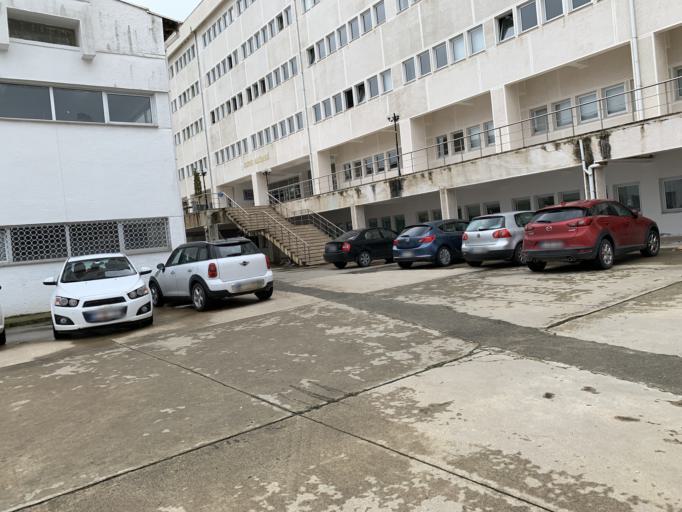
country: TR
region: Trabzon
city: Trabzon
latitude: 40.9928
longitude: 39.7741
